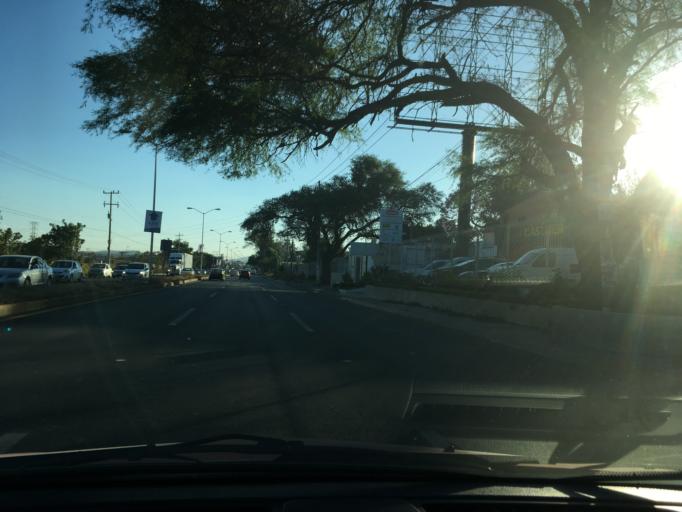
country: MX
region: Jalisco
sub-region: Tlajomulco de Zuniga
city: La Tijera
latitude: 20.5829
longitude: -103.4258
